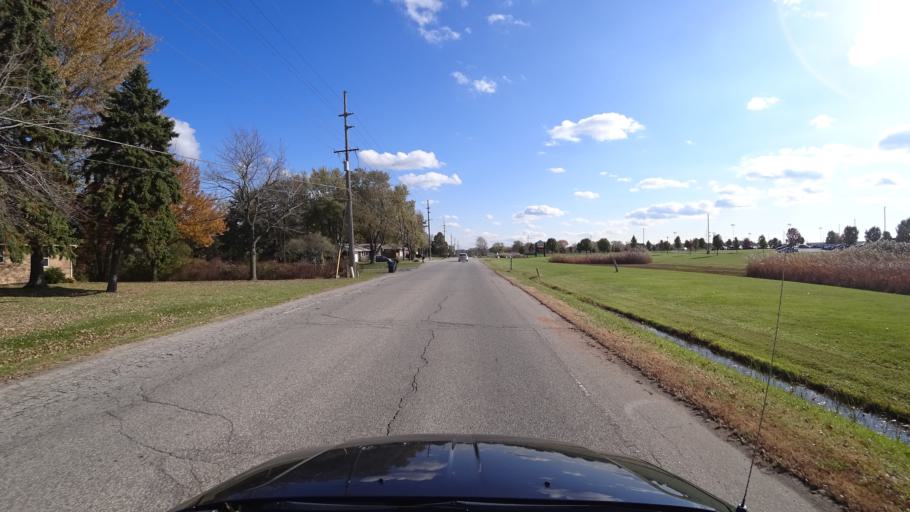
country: US
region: Indiana
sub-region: LaPorte County
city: Trail Creek
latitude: 41.6802
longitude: -86.8643
